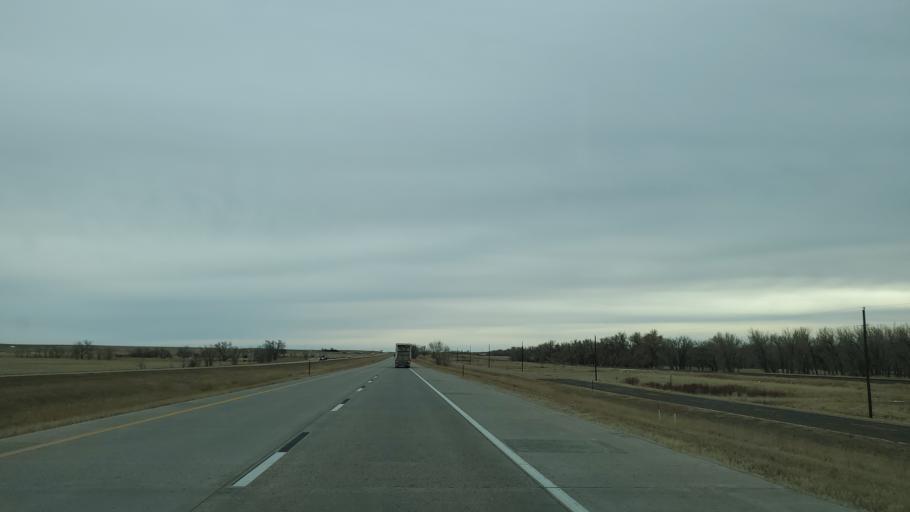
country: US
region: Colorado
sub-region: Arapahoe County
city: Byers
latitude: 39.5729
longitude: -104.0187
